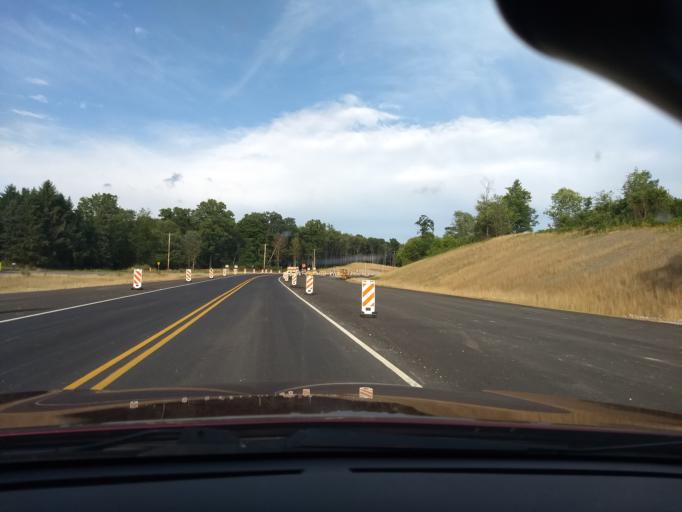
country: US
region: Pennsylvania
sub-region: Armstrong County
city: Freeport
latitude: 40.6633
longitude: -79.6845
